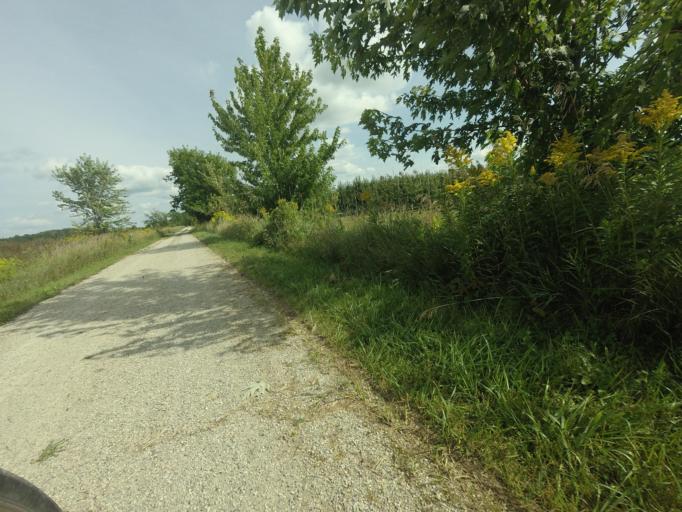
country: CA
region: Ontario
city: Waterloo
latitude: 43.5986
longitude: -80.5016
